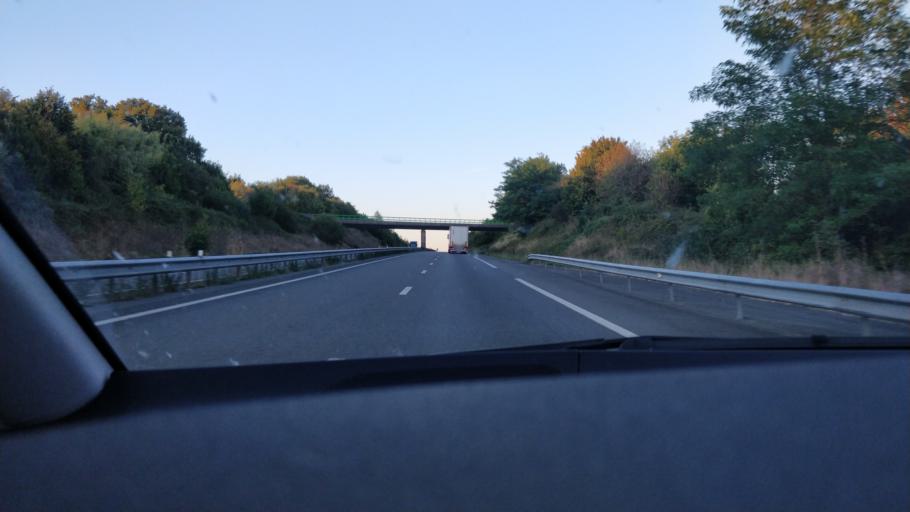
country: FR
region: Poitou-Charentes
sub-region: Departement de la Charente
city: Chasseneuil-sur-Bonnieure
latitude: 45.8054
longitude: 0.4430
